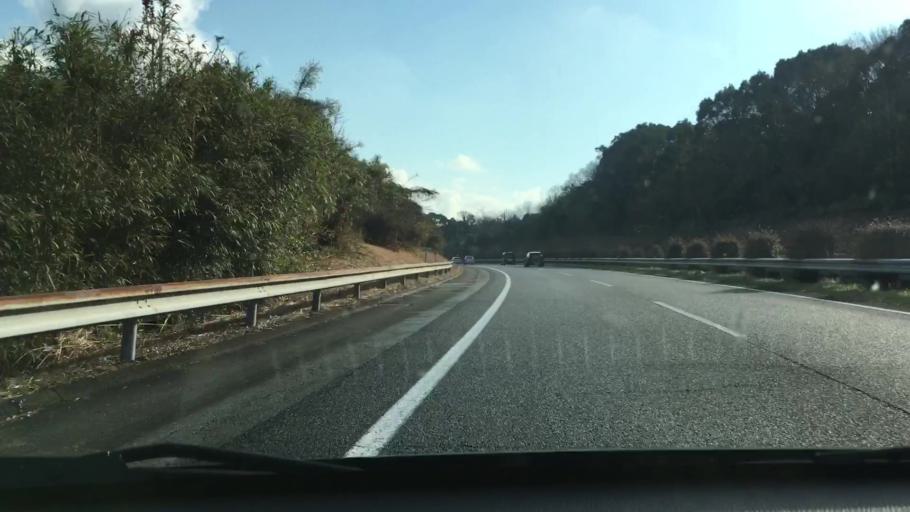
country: JP
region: Kumamoto
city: Matsubase
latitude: 32.6423
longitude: 130.7067
